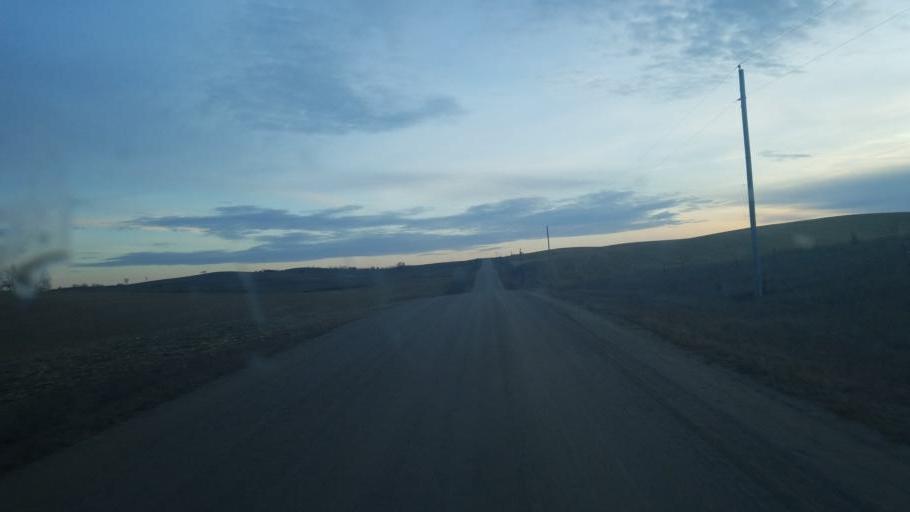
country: US
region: Nebraska
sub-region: Knox County
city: Center
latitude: 42.6773
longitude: -97.7599
